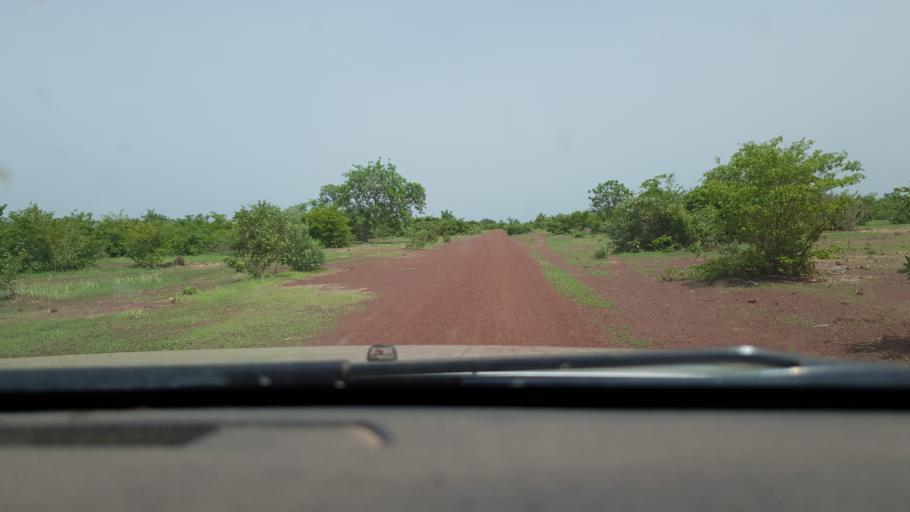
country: ML
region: Koulikoro
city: Koulikoro
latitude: 12.6660
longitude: -7.2304
